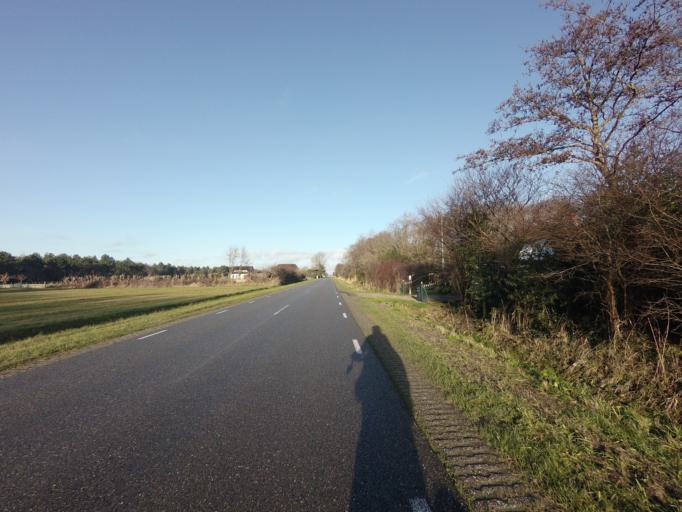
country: NL
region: North Holland
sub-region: Gemeente Texel
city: Den Burg
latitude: 53.1522
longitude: 4.8653
